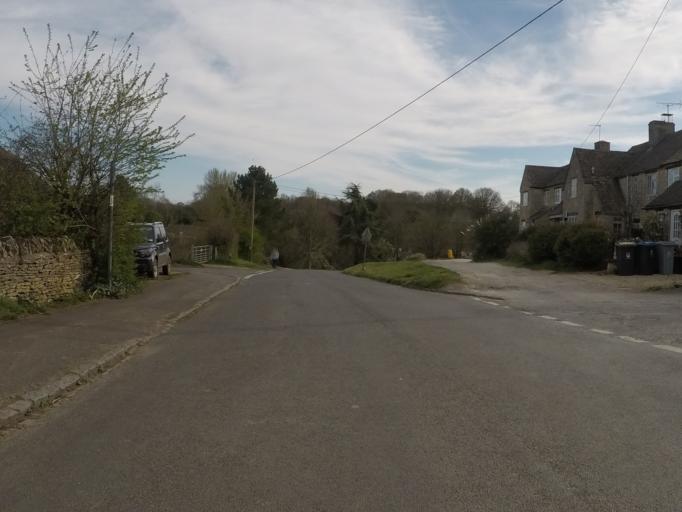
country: GB
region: England
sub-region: Oxfordshire
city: Charlbury
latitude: 51.8444
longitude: -1.4767
